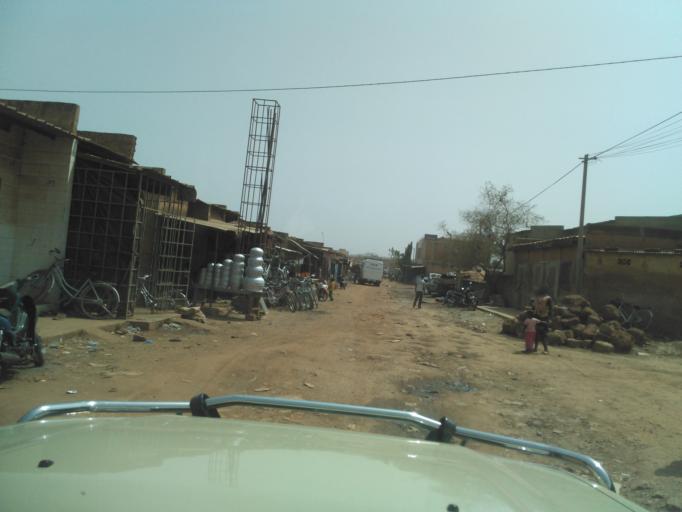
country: BF
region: Centre
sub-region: Kadiogo Province
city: Ouagadougou
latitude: 12.3894
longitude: -1.5658
